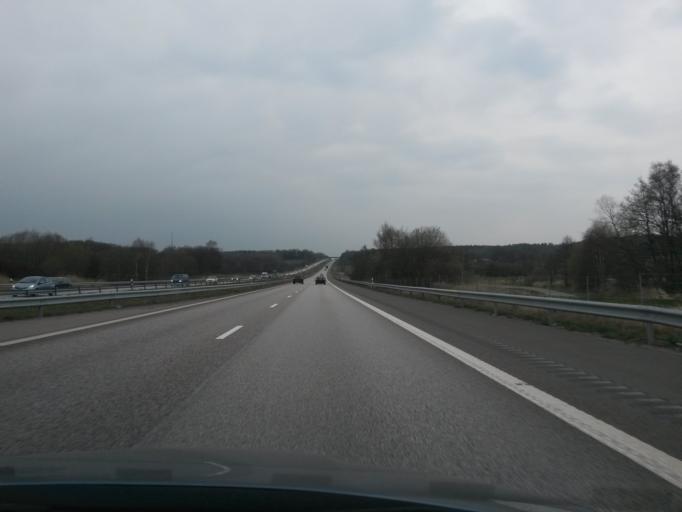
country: SE
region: Halland
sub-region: Kungsbacka Kommun
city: Frillesas
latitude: 57.2589
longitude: 12.2165
